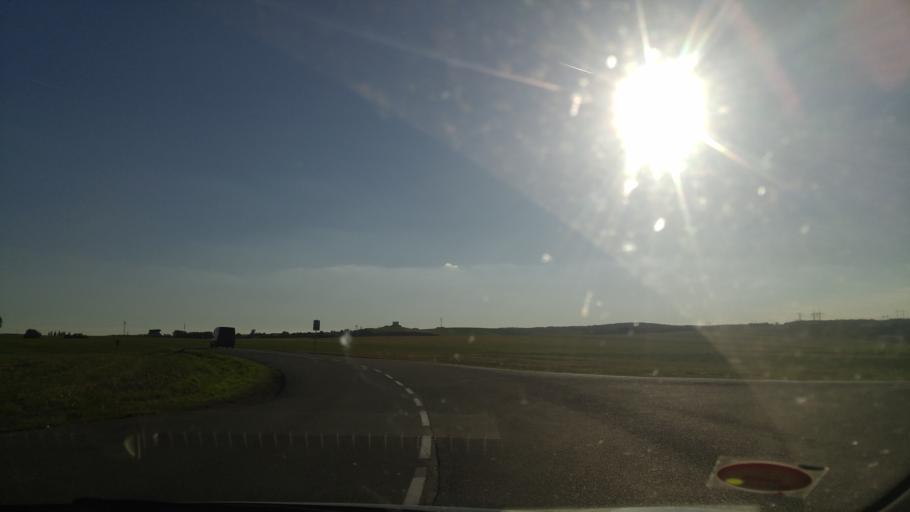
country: CZ
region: South Moravian
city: Ricany
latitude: 49.2275
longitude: 16.4188
